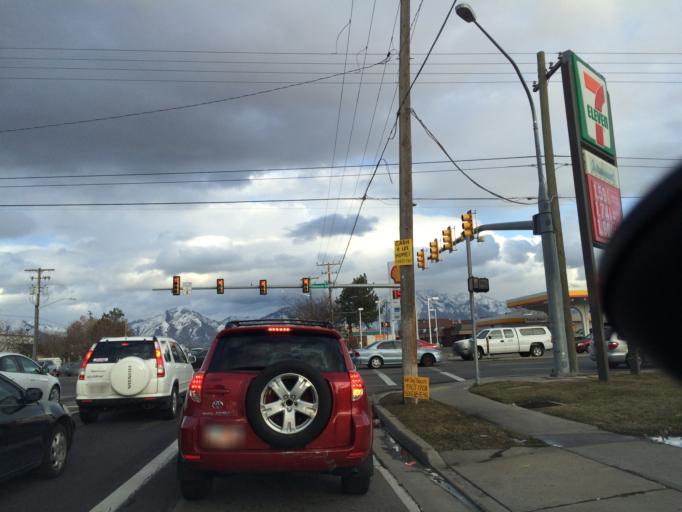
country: US
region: Utah
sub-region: Salt Lake County
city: Taylorsville
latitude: 40.6820
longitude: -111.9393
